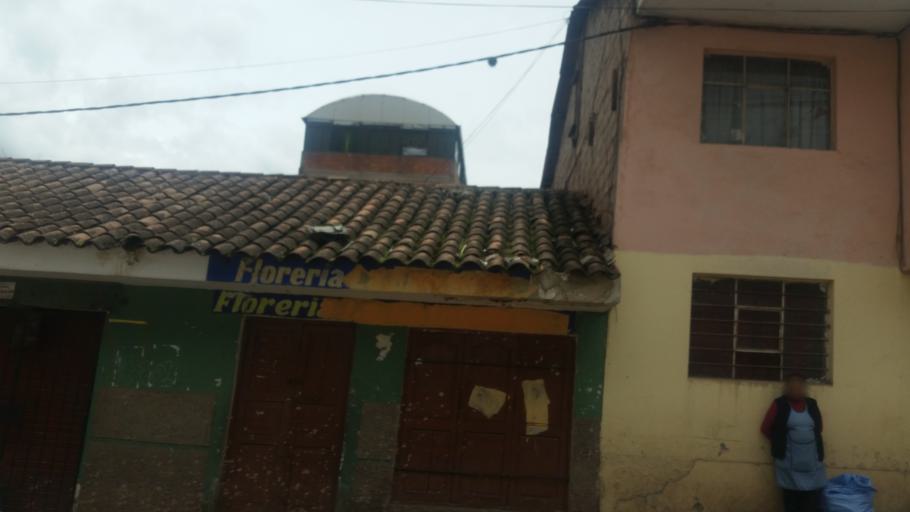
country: PE
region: Cusco
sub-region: Provincia de Cusco
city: Cusco
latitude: -13.5251
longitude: -71.9806
